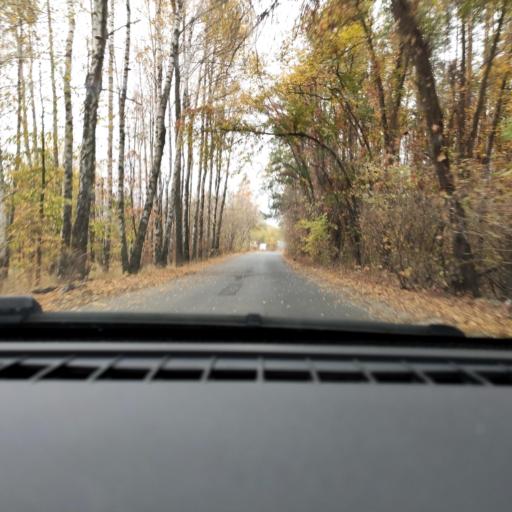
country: RU
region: Voronezj
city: Somovo
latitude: 51.6846
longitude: 39.2992
